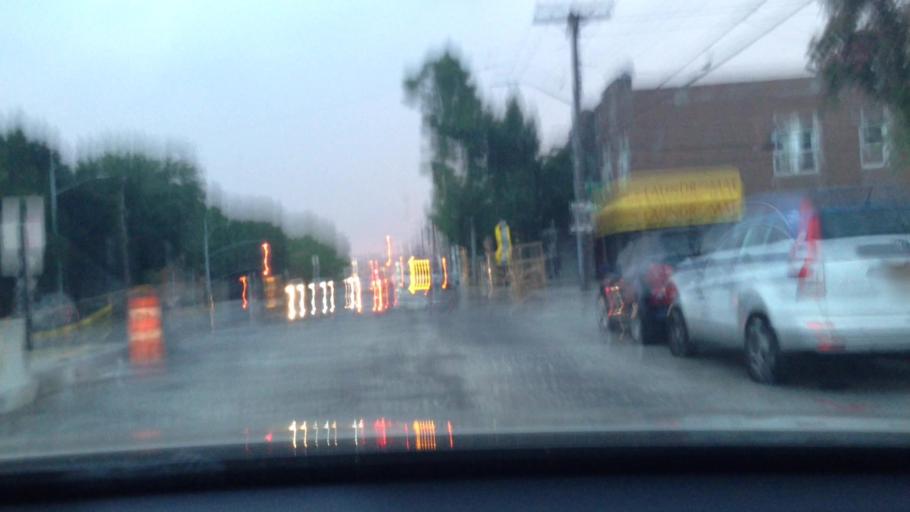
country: US
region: New York
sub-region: Kings County
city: East New York
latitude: 40.6469
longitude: -73.8956
